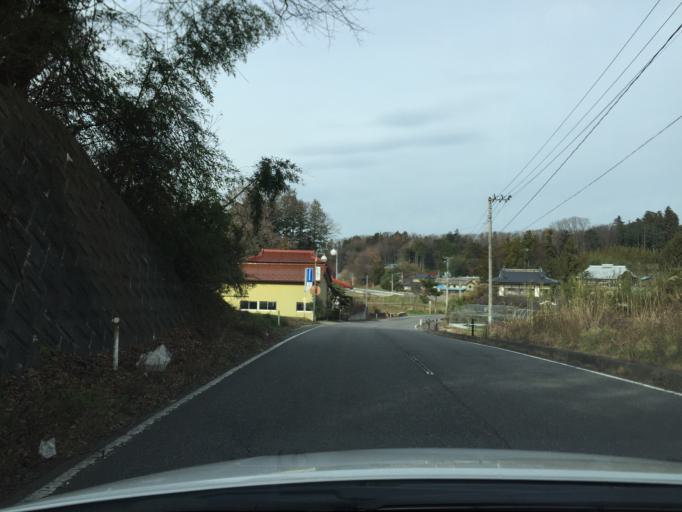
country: JP
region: Fukushima
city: Funehikimachi-funehiki
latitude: 37.4039
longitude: 140.5924
